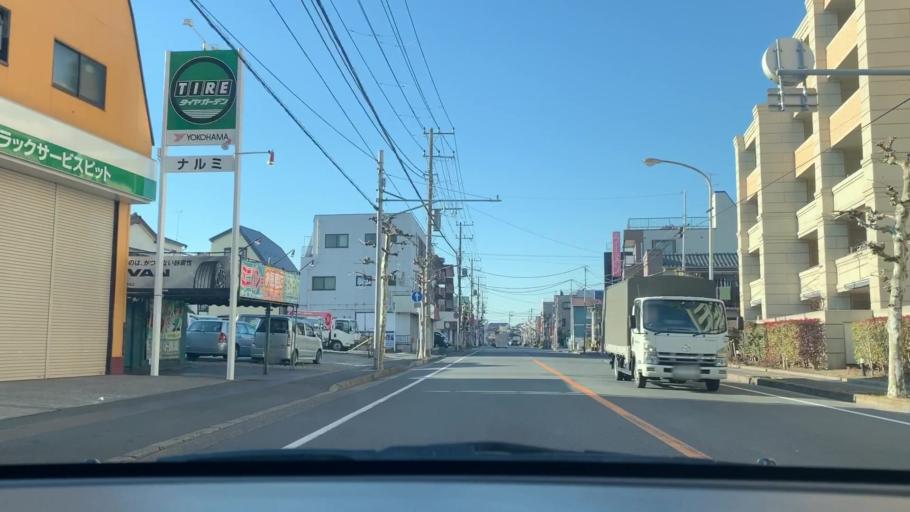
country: JP
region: Tokyo
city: Urayasu
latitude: 35.7154
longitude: 139.9148
